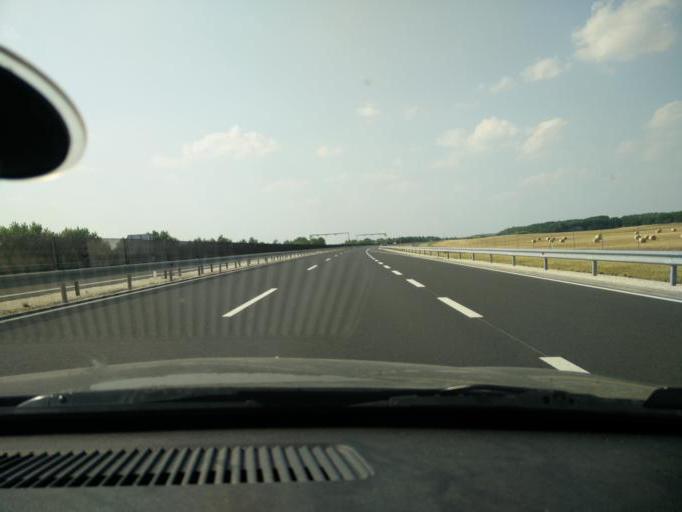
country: HU
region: Tolna
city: Szedres
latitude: 46.4435
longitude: 18.7074
